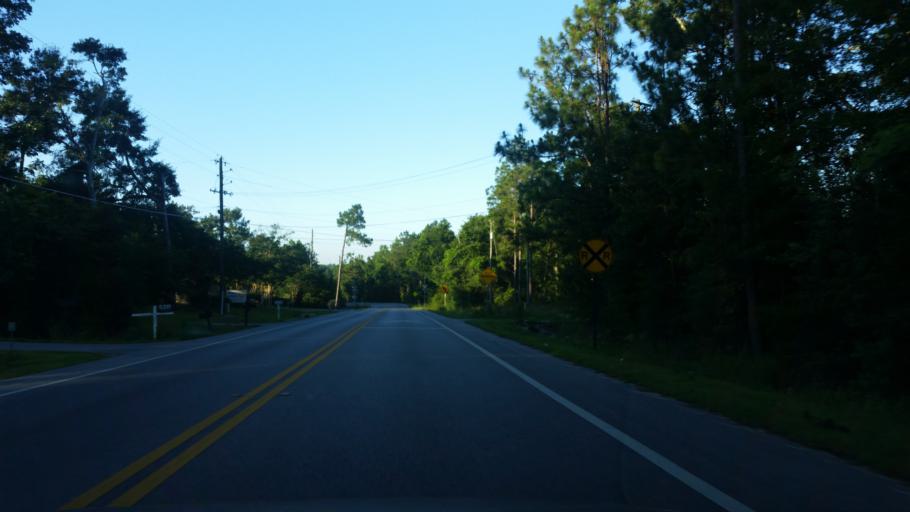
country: US
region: Florida
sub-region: Escambia County
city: Cantonment
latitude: 30.6053
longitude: -87.3573
